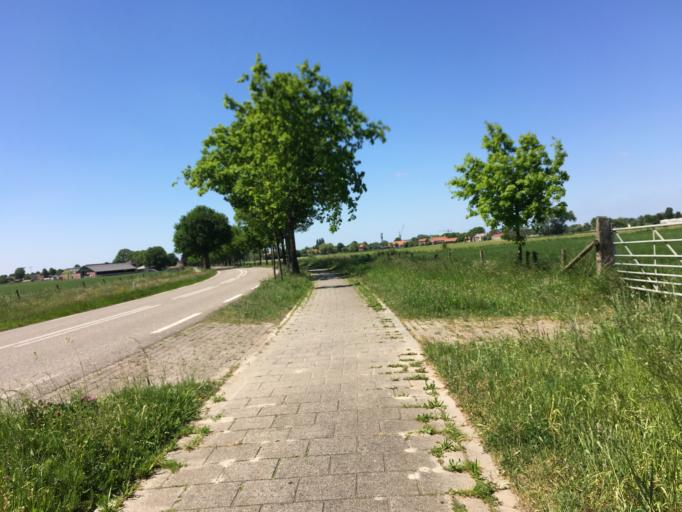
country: NL
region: North Brabant
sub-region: Gemeente Heusden
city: Heusden
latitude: 51.7301
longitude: 5.1704
